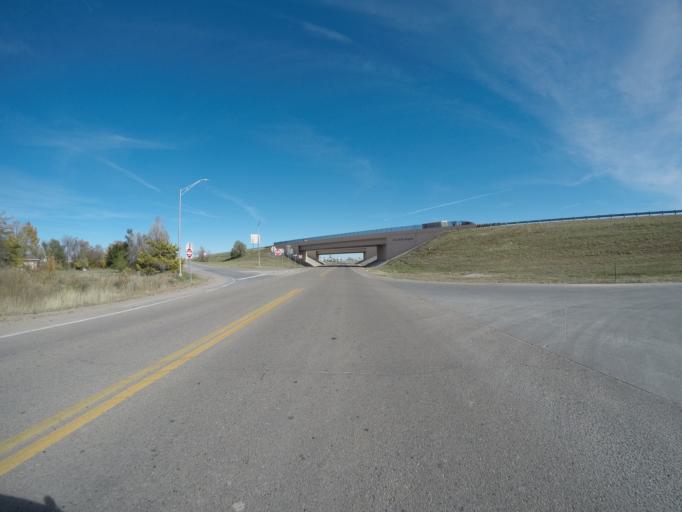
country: US
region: Colorado
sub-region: Kit Carson County
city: Burlington
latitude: 39.3011
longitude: -102.2564
